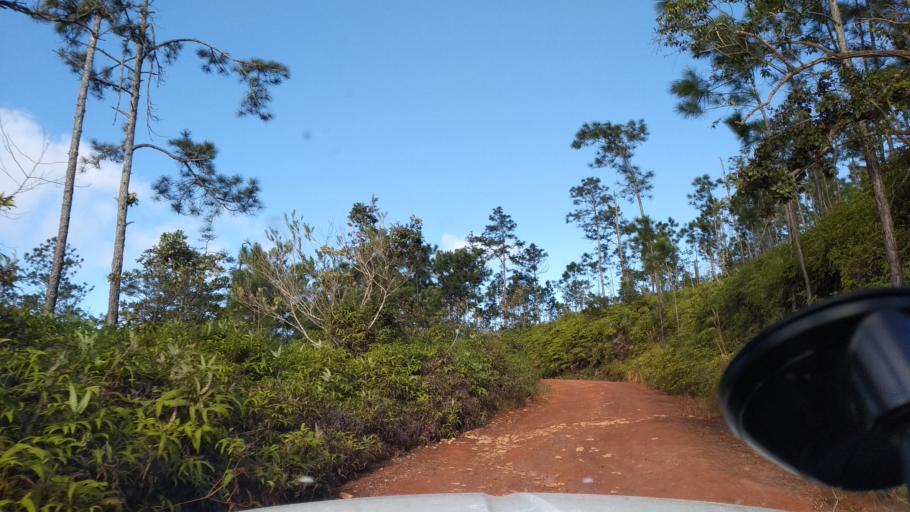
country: BZ
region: Cayo
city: Belmopan
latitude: 16.9981
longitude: -88.8310
